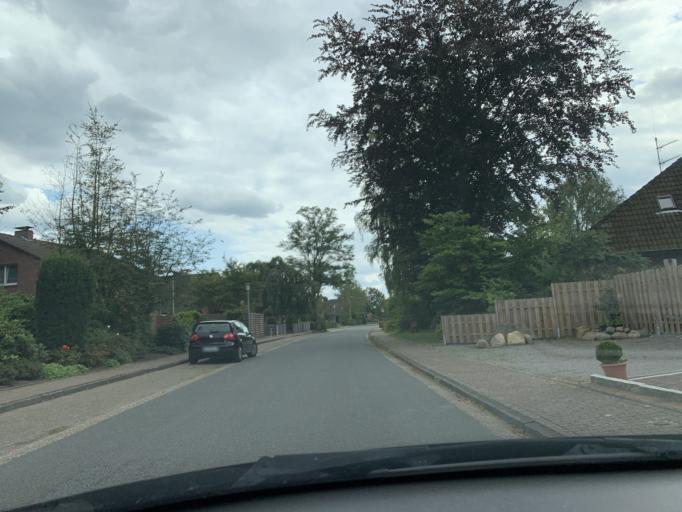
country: DE
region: Lower Saxony
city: Westerstede
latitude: 53.2562
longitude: 7.9416
